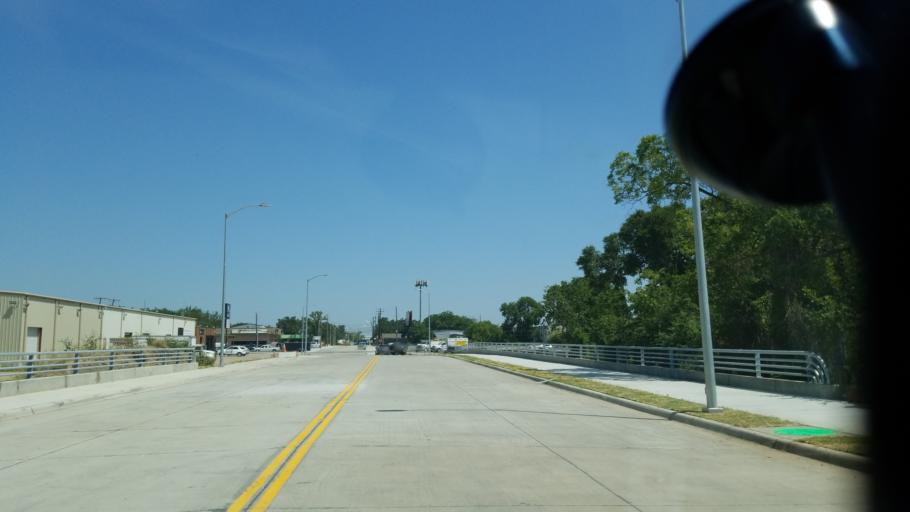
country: US
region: Texas
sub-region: Dallas County
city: Farmers Branch
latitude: 32.8940
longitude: -96.9020
